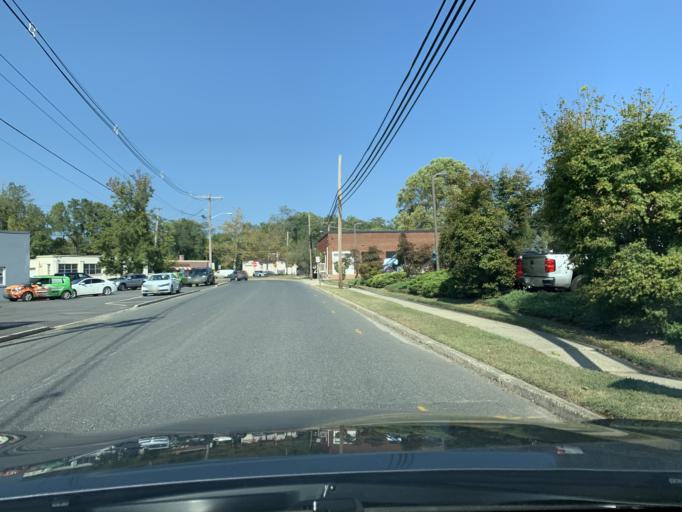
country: US
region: New Jersey
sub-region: Monmouth County
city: Eatontown
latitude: 40.3013
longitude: -74.0665
